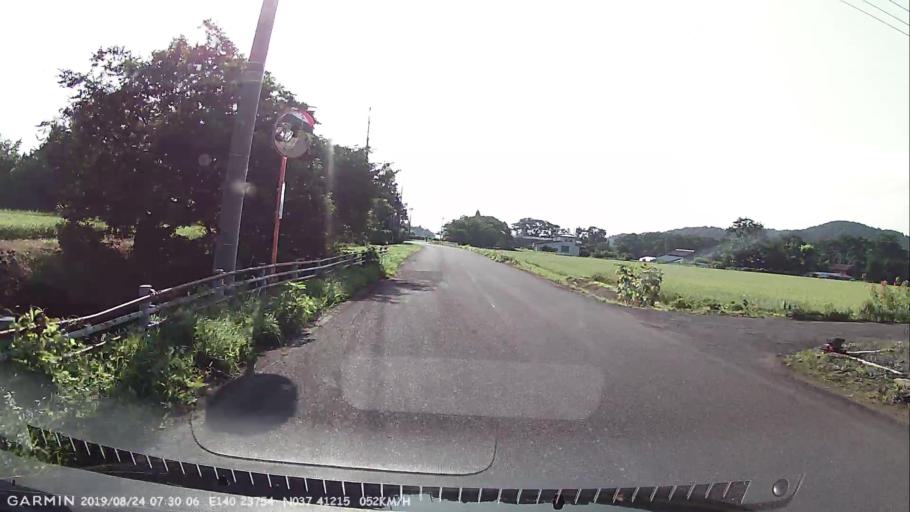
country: JP
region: Fukushima
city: Koriyama
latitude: 37.4121
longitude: 140.2377
